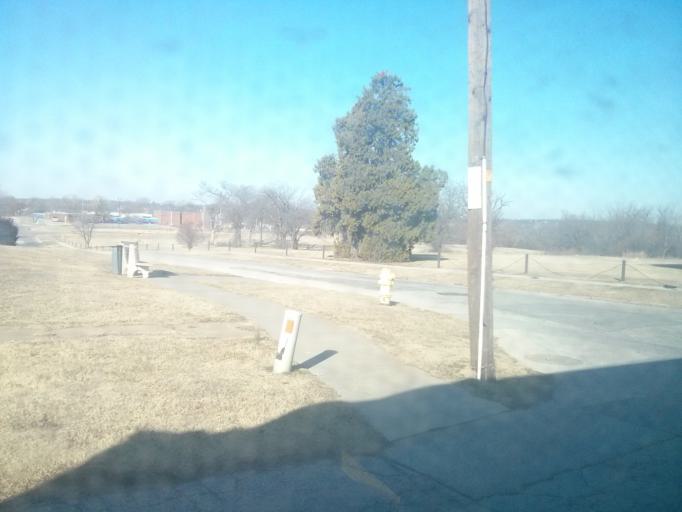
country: US
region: Oklahoma
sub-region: Tulsa County
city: Tulsa
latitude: 36.1669
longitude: -95.9912
